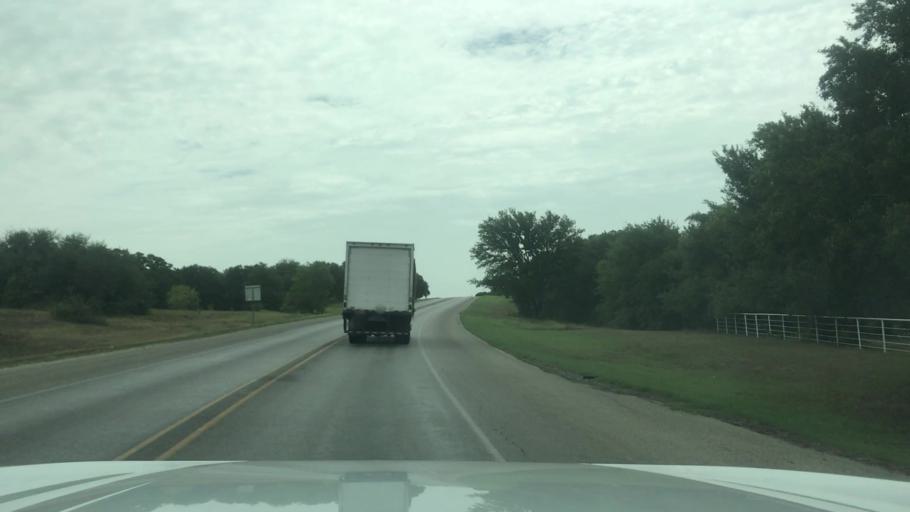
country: US
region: Texas
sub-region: Comanche County
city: De Leon
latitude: 32.1075
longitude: -98.4921
